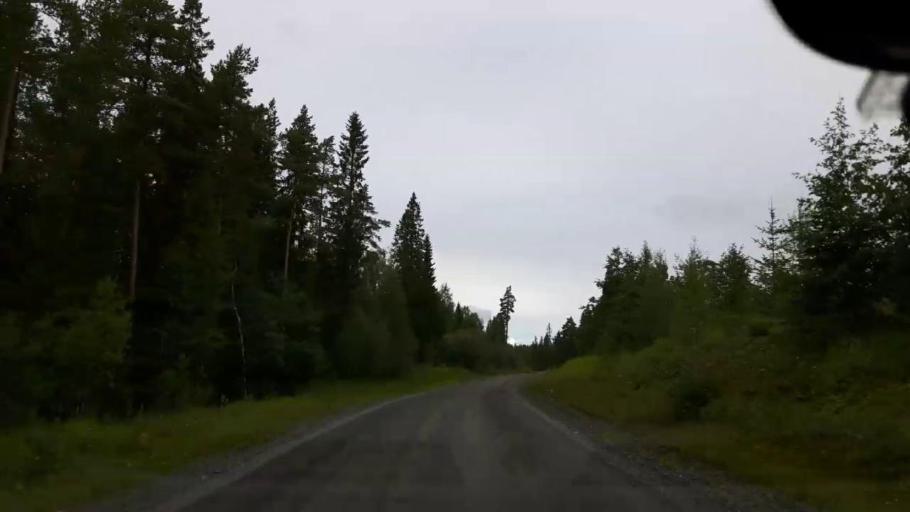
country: SE
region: Jaemtland
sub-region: Krokoms Kommun
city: Krokom
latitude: 63.2994
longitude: 14.3569
